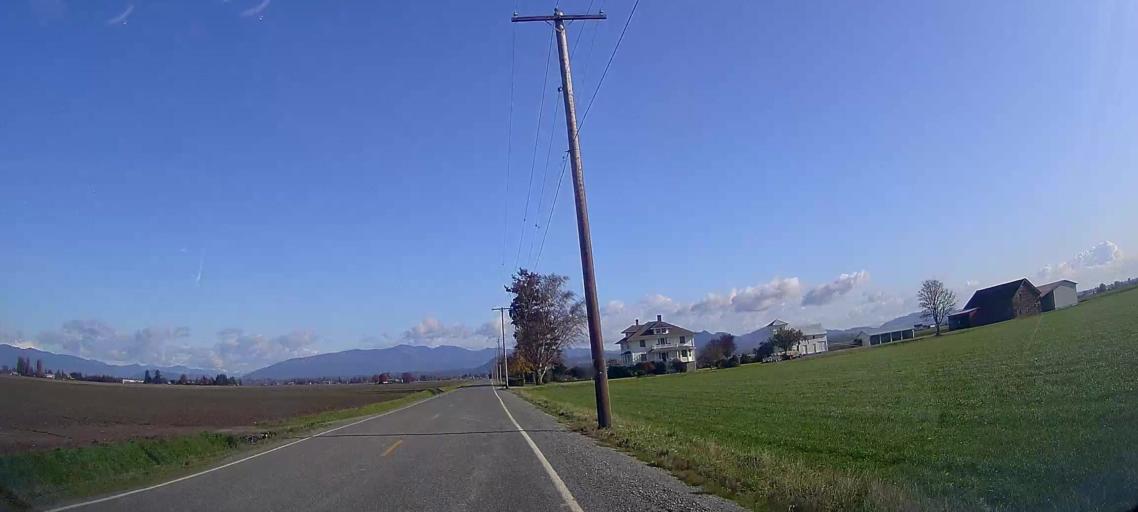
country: US
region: Washington
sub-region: Skagit County
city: Mount Vernon
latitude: 48.3990
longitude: -122.4342
